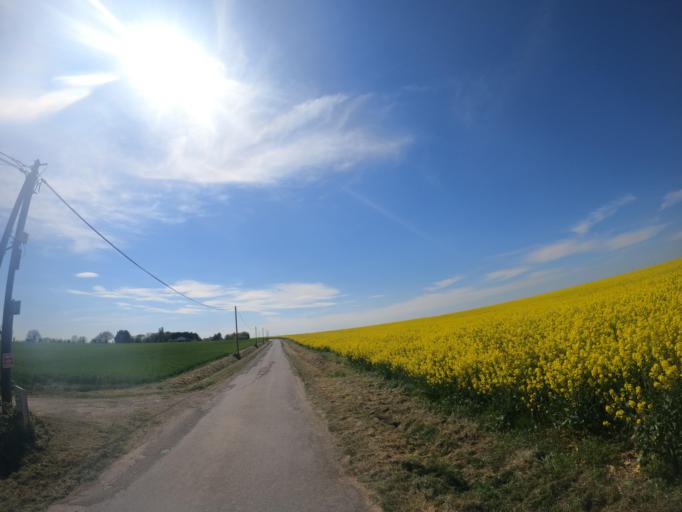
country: FR
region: Poitou-Charentes
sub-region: Departement des Deux-Sevres
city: Airvault
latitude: 46.8855
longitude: -0.1521
